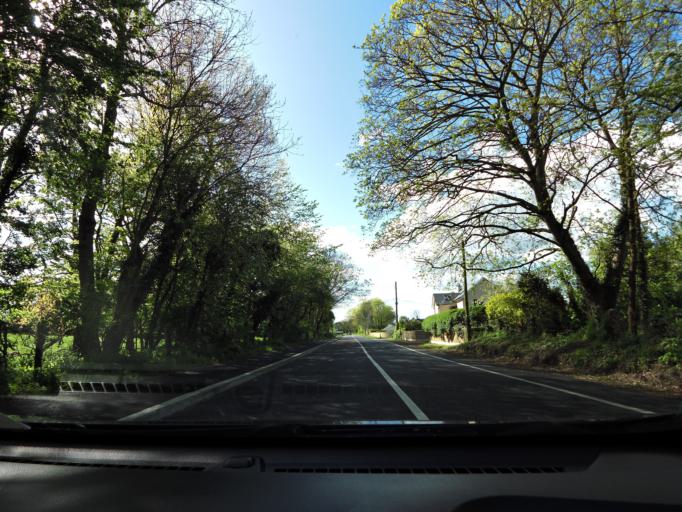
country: IE
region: Leinster
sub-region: Kildare
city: Maynooth
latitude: 53.3820
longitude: -6.6188
